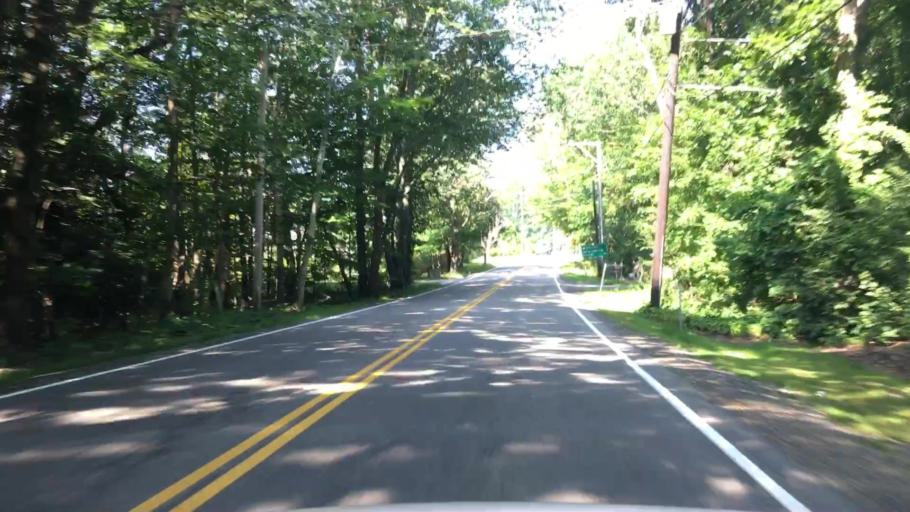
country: US
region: New Hampshire
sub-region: Rockingham County
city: Kensington
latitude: 42.9066
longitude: -70.9223
